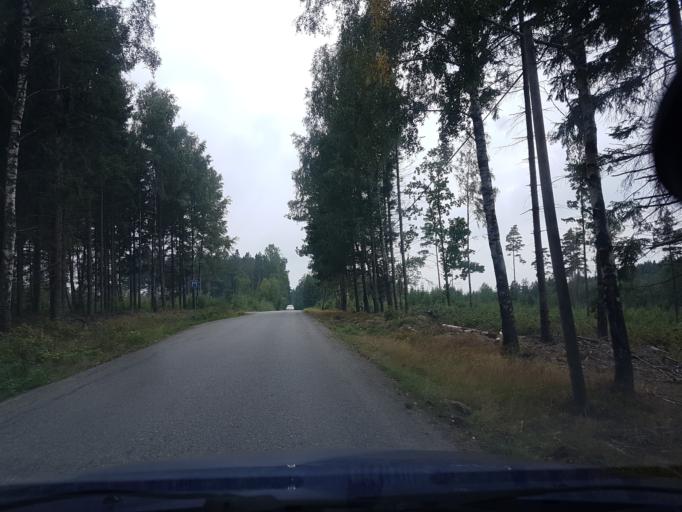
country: SE
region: Vaestra Goetaland
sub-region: Harryda Kommun
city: Landvetter
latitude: 57.7181
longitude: 12.2274
